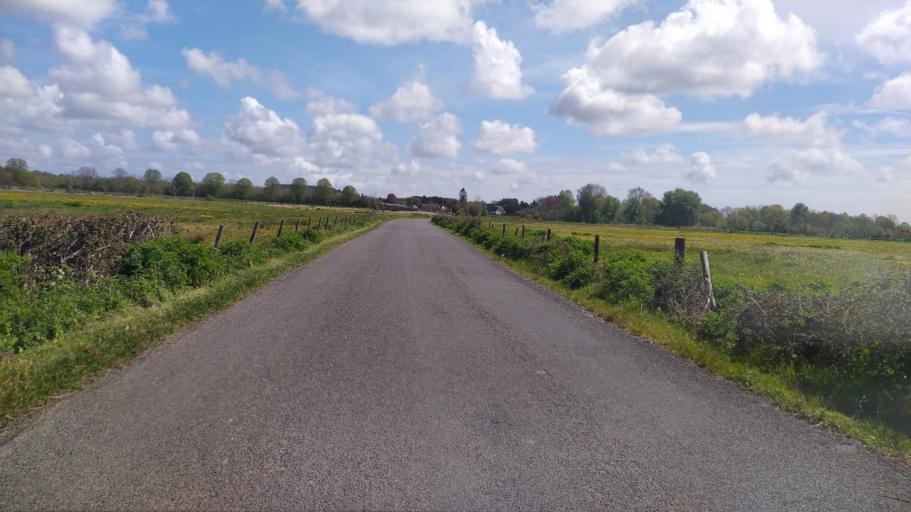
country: GB
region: England
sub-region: Hampshire
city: Fordingbridge
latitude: 50.8893
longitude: -1.7932
